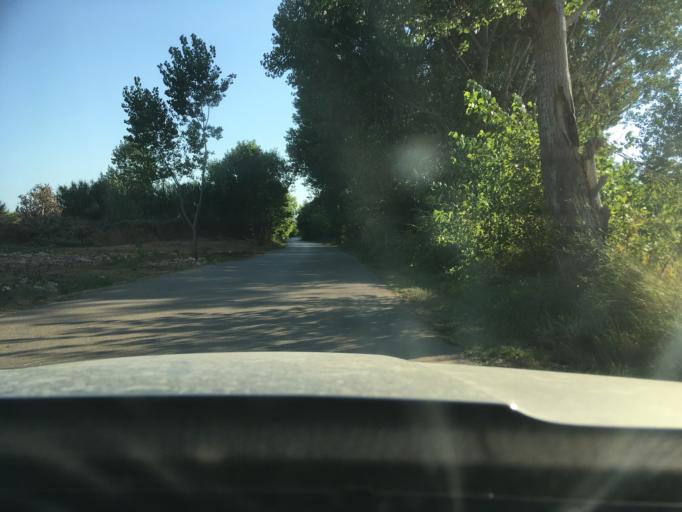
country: HR
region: Zadarska
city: Privlaka
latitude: 44.2511
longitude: 15.1526
